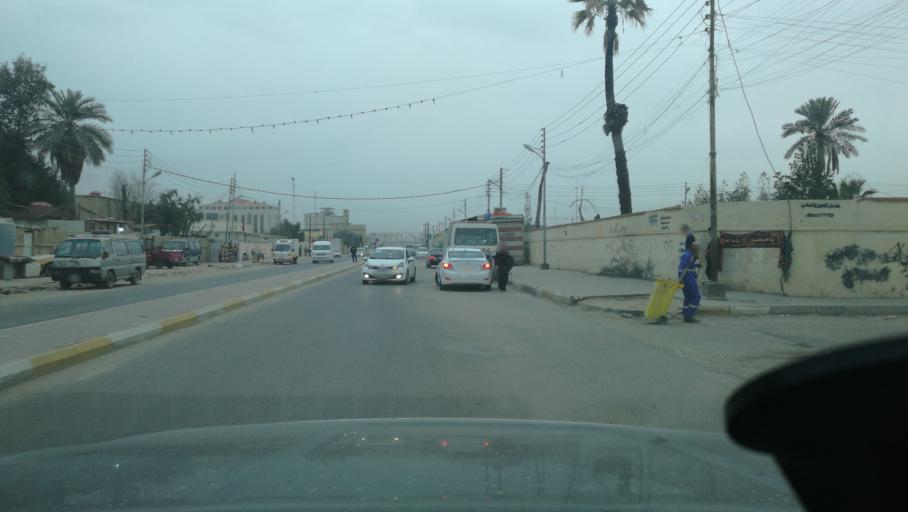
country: IQ
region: Basra Governorate
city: Al Basrah al Qadimah
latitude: 30.5096
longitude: 47.8379
